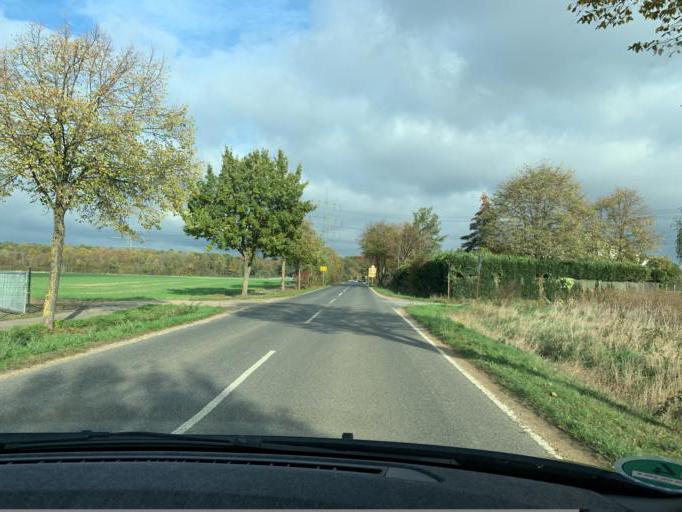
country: DE
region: North Rhine-Westphalia
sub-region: Regierungsbezirk Koln
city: Niederzier
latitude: 50.8752
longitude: 6.4803
